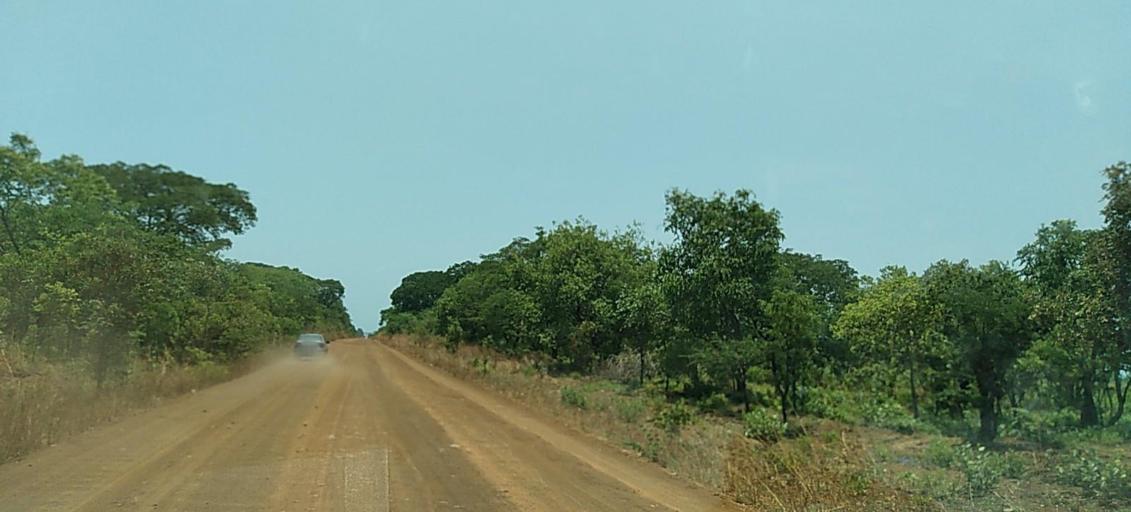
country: ZM
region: Copperbelt
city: Mpongwe
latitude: -13.6900
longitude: 27.8616
